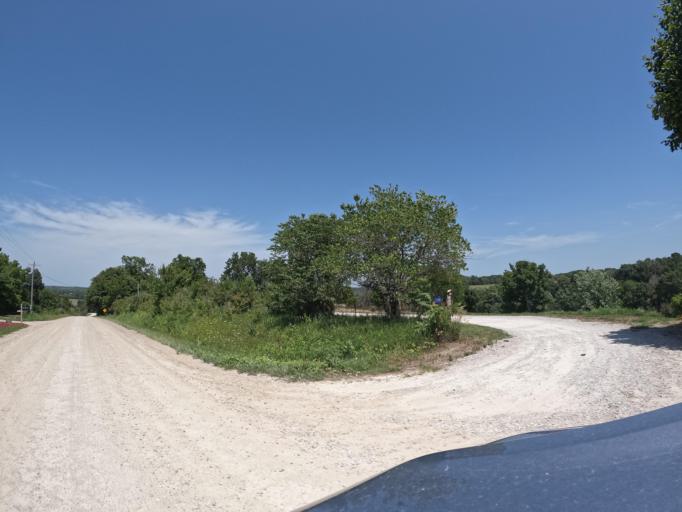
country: US
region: Iowa
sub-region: Henry County
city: Mount Pleasant
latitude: 40.9619
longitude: -91.6727
